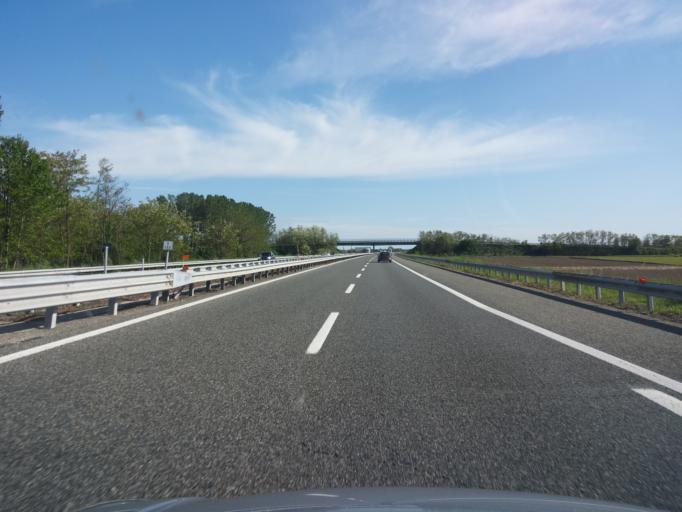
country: IT
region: Piedmont
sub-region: Provincia di Novara
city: Landiona
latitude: 45.4995
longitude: 8.4379
